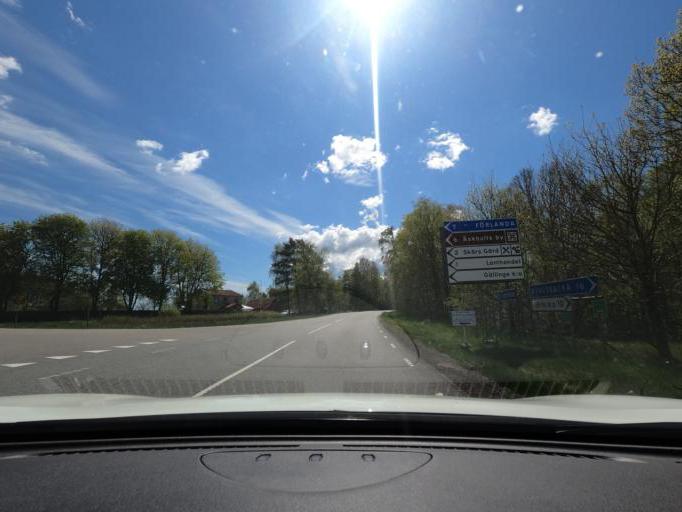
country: SE
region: Halland
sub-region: Kungsbacka Kommun
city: Fjaeras kyrkby
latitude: 57.3933
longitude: 12.2472
